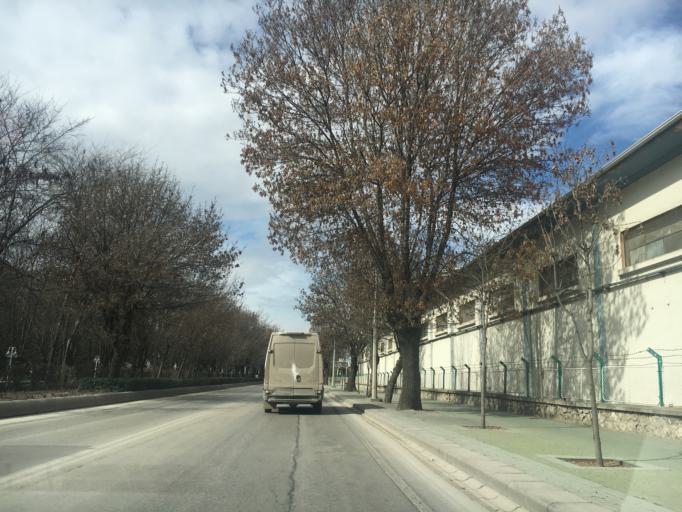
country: TR
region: Eskisehir
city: Eskisehir
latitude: 39.7768
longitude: 30.5416
